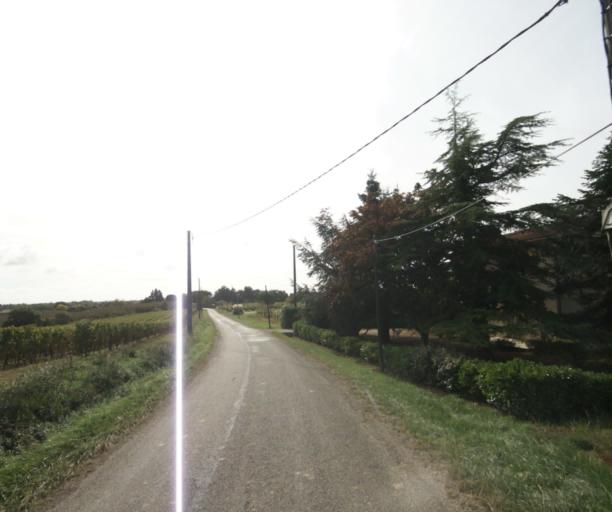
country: FR
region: Midi-Pyrenees
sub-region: Departement du Gers
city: Eauze
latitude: 43.8679
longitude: 0.1262
